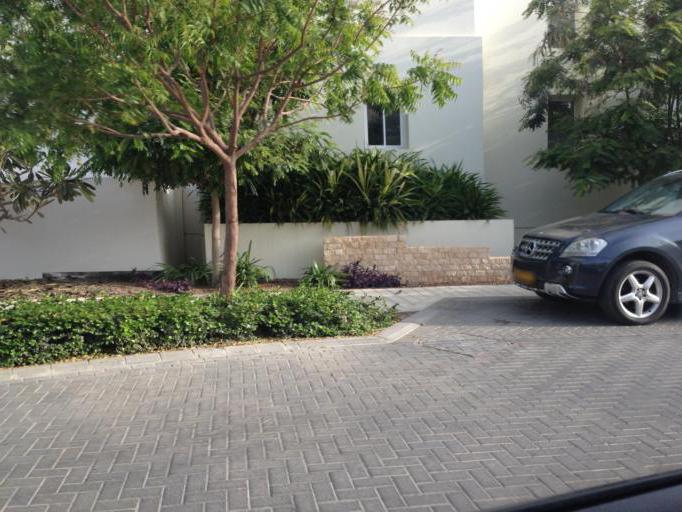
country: OM
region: Muhafazat Masqat
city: As Sib al Jadidah
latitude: 23.6288
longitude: 58.2697
